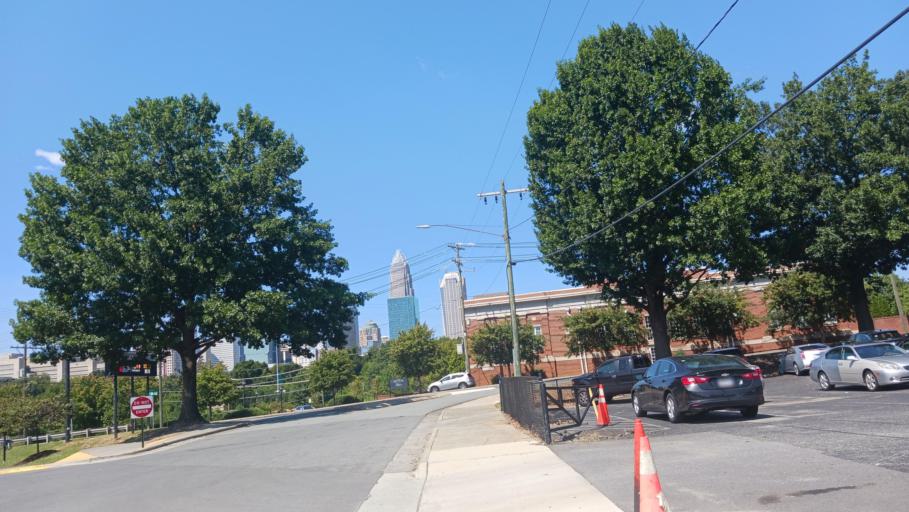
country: US
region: North Carolina
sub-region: Mecklenburg County
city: Charlotte
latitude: 35.2196
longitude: -80.8288
